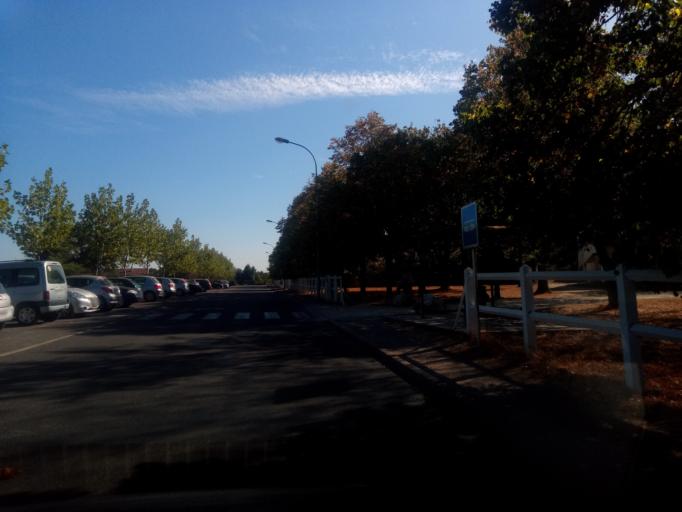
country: FR
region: Poitou-Charentes
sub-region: Departement de la Vienne
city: Montmorillon
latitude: 46.4166
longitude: 0.8440
